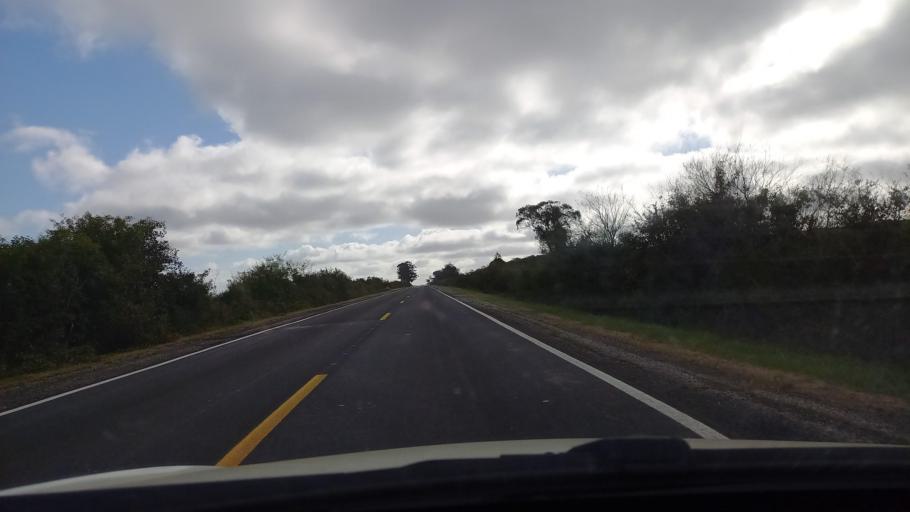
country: BR
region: Rio Grande do Sul
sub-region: Dom Pedrito
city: Dom Pedrito
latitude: -30.8950
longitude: -54.8500
